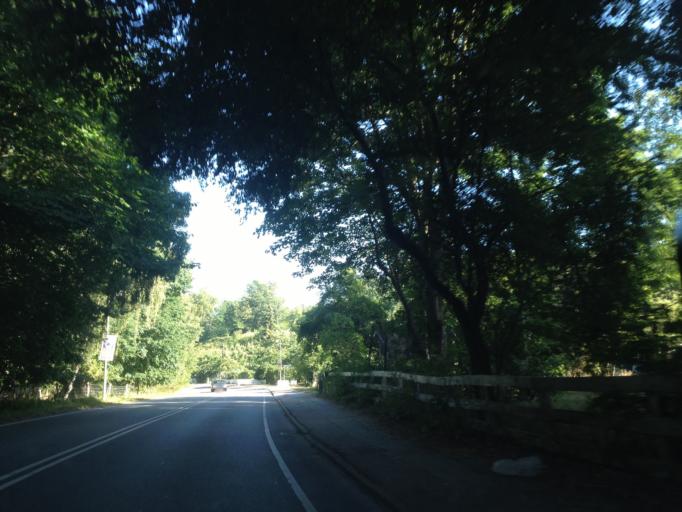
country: DK
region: Capital Region
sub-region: Gribskov Kommune
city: Helsinge
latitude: 56.0533
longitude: 12.1051
